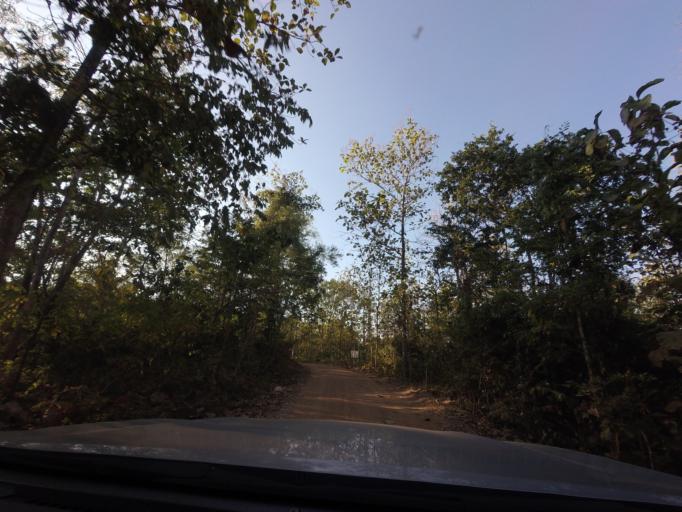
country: TH
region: Lampang
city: Mae Mo
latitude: 18.4137
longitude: 99.7447
